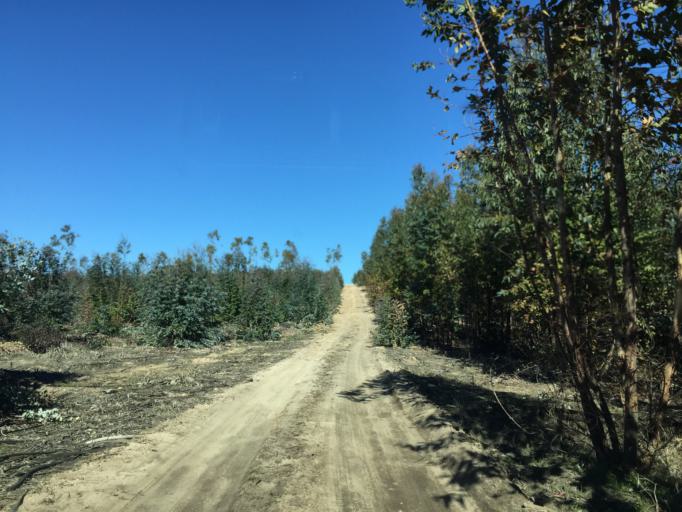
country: PT
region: Portalegre
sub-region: Nisa
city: Nisa
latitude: 39.4908
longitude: -7.7718
